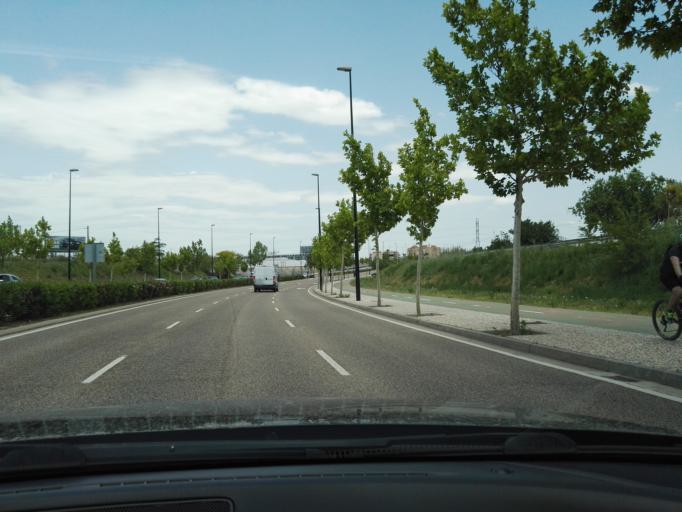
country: ES
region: Aragon
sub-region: Provincia de Zaragoza
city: Zaragoza
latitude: 41.6286
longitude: -0.8687
